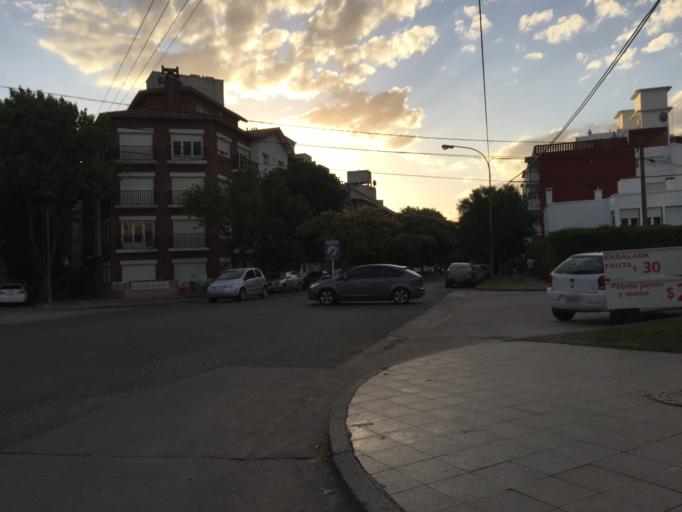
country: AR
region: Buenos Aires
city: Miramar
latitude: -38.2703
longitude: -57.8328
